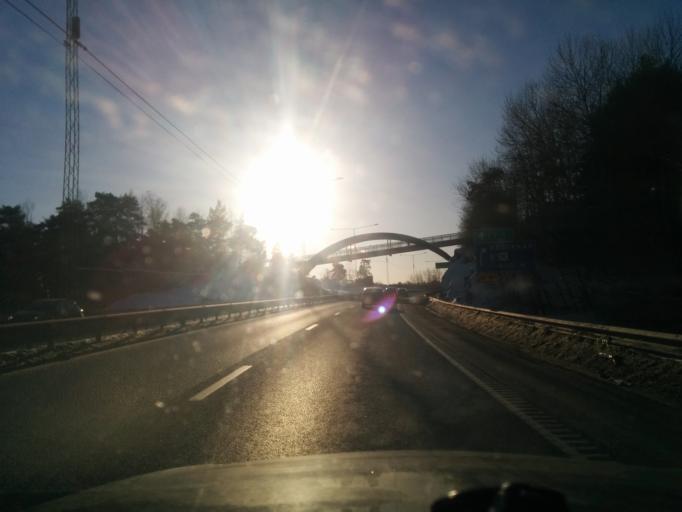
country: SE
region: Stockholm
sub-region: Taby Kommun
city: Taby
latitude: 59.4489
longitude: 18.1296
